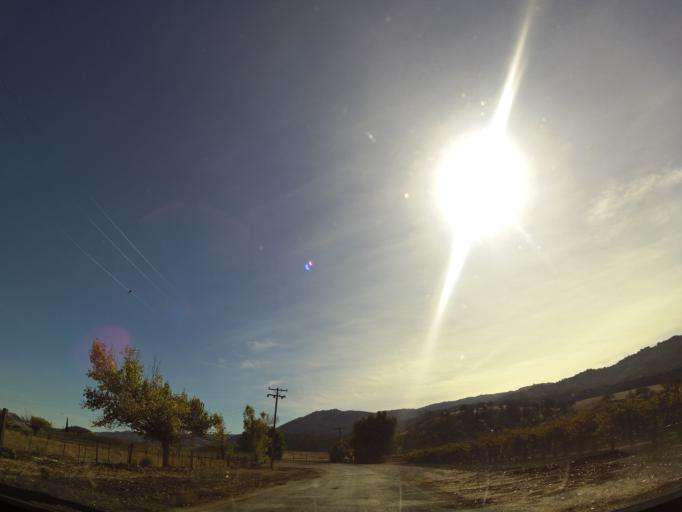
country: US
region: California
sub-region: San Benito County
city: Ridgemark
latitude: 36.6672
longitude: -121.2542
